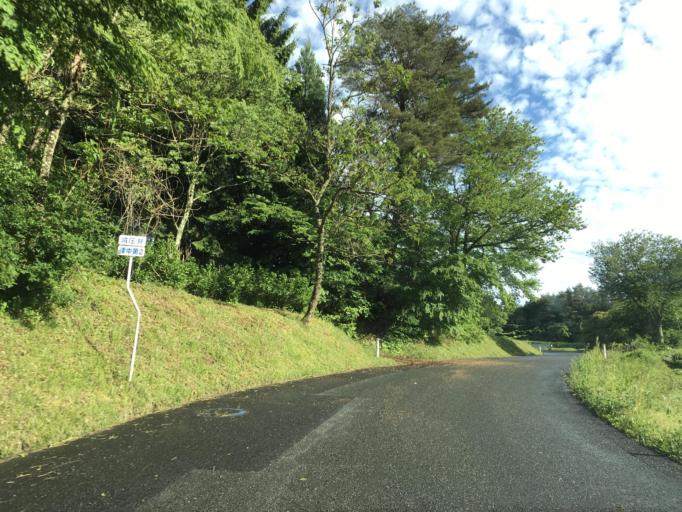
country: JP
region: Iwate
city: Ichinoseki
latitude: 38.8649
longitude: 141.4259
